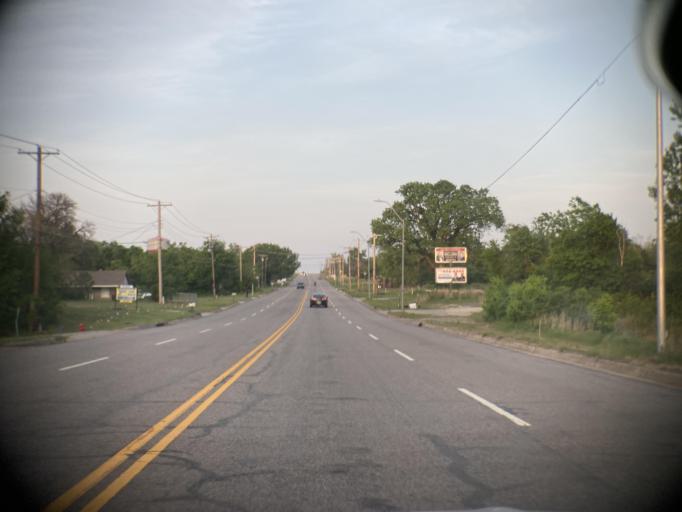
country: US
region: Oklahoma
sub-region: Oklahoma County
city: Midwest City
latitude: 35.4352
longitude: -97.3655
